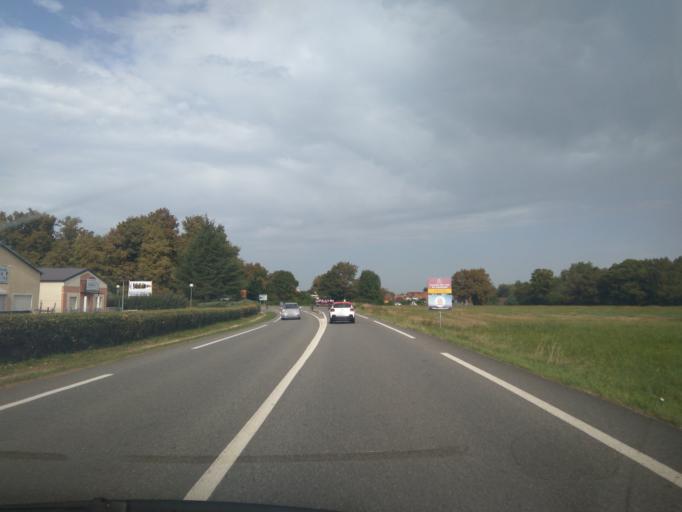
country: FR
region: Aquitaine
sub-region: Departement des Pyrenees-Atlantiques
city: Artiguelouve
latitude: 43.3129
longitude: -0.4516
